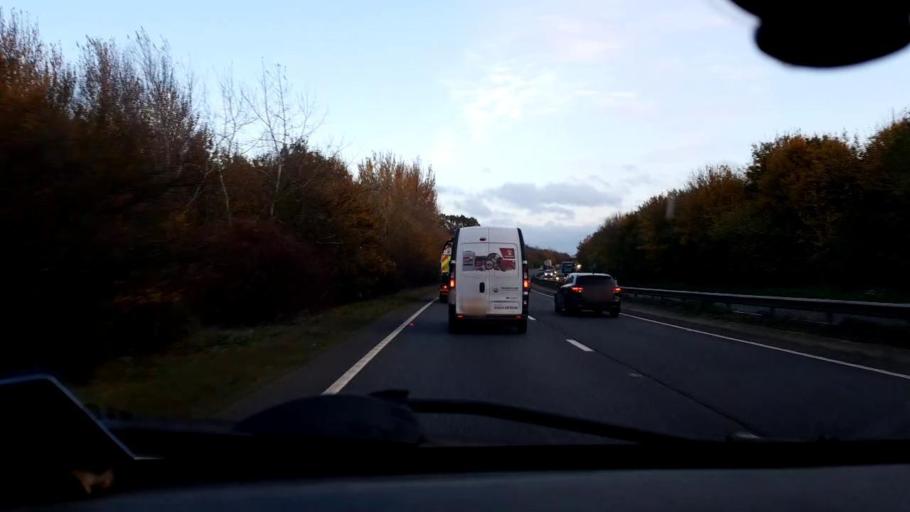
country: GB
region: England
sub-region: Norfolk
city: Bowthorpe
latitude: 52.6210
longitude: 1.2049
